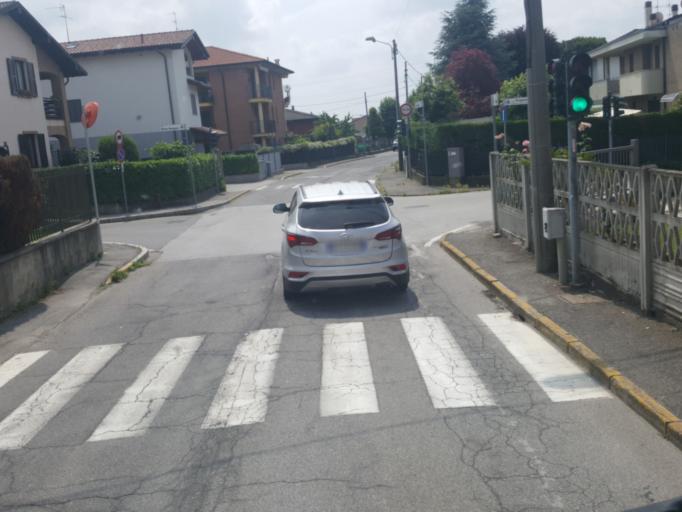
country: IT
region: Lombardy
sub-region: Provincia di Como
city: Novedrate
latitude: 45.6937
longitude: 9.1246
